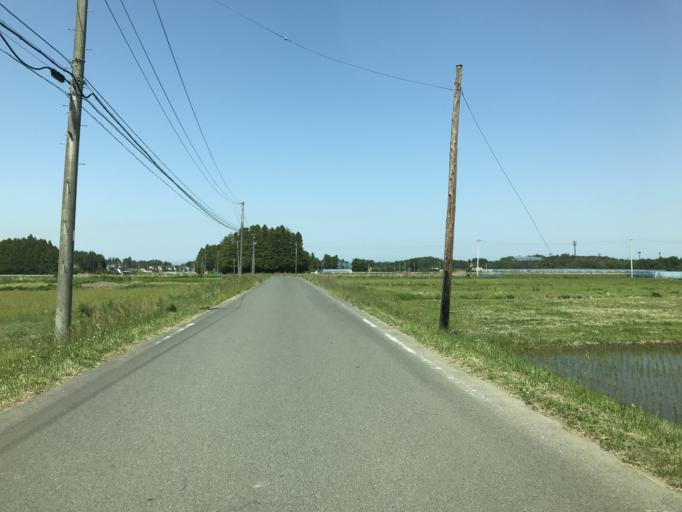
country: JP
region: Miyagi
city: Marumori
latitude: 37.8602
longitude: 140.9061
